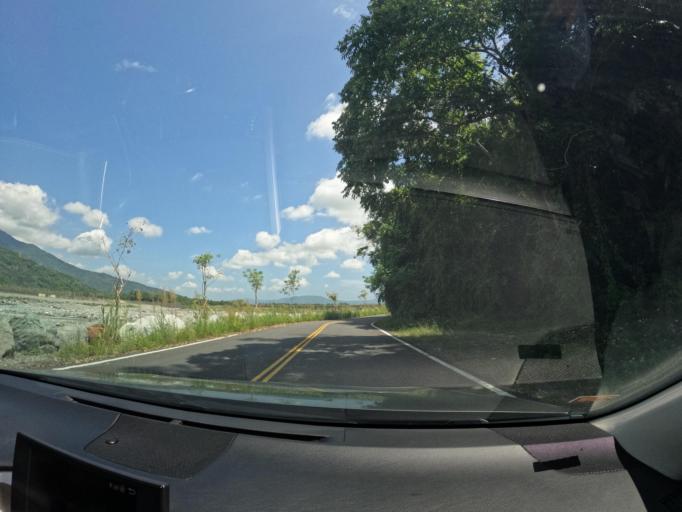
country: TW
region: Taiwan
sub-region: Hualien
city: Hualian
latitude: 23.6866
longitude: 121.4044
